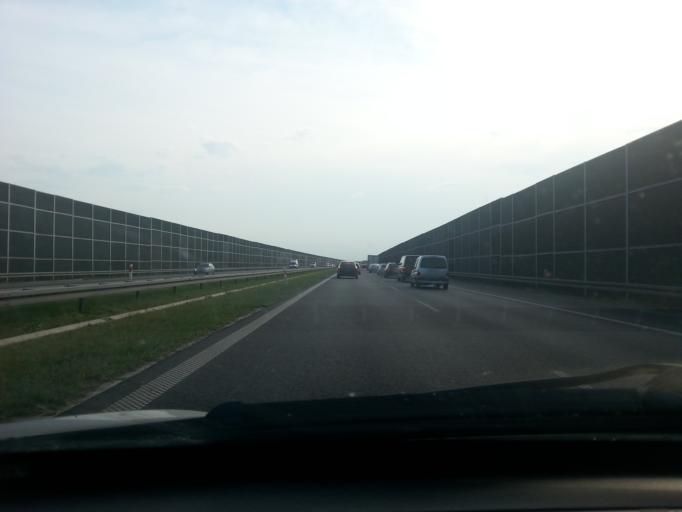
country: PL
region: Masovian Voivodeship
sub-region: Powiat pruszkowski
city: Otrebusy
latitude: 52.1704
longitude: 20.7510
